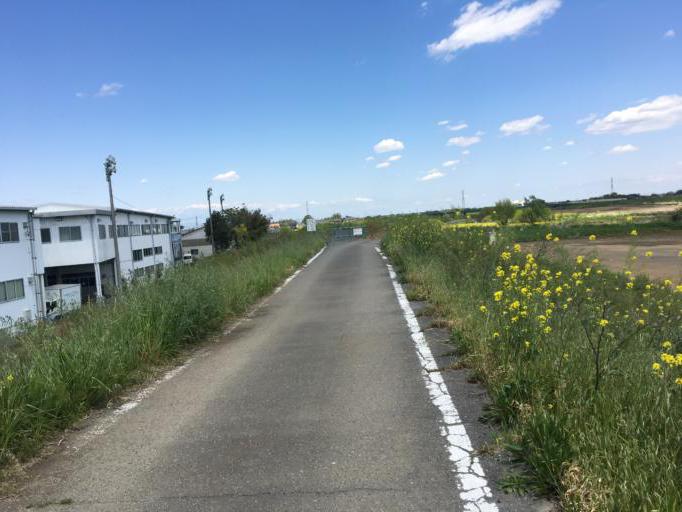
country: JP
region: Saitama
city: Kawagoe
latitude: 35.9355
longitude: 139.4624
